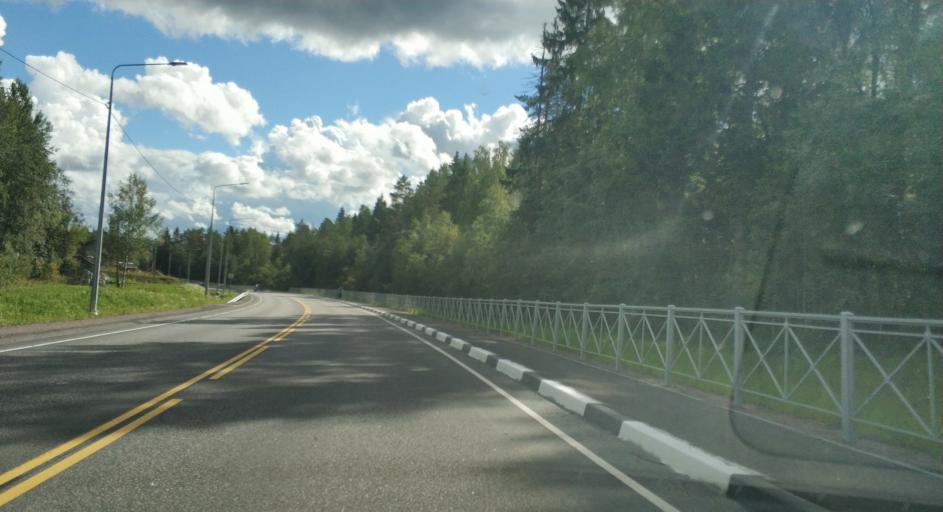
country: RU
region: Republic of Karelia
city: Ruskeala
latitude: 61.9274
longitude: 30.5993
